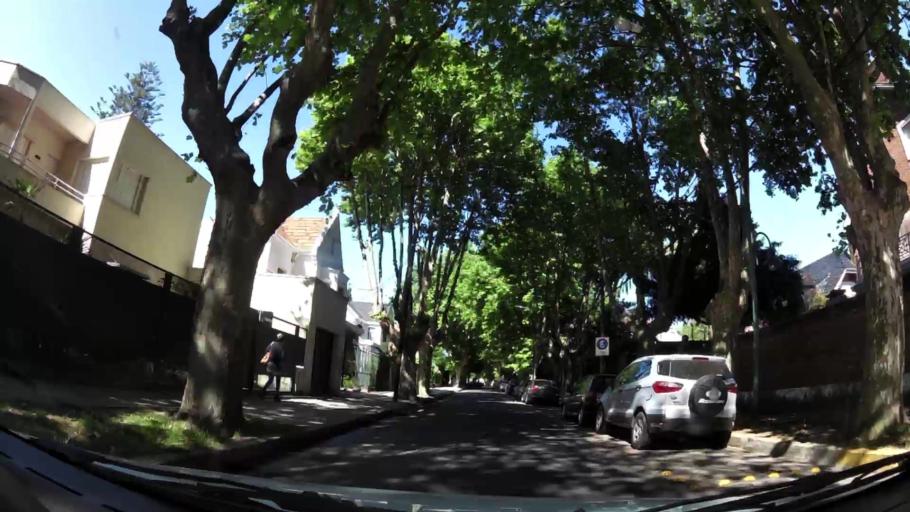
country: AR
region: Buenos Aires
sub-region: Partido de Vicente Lopez
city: Olivos
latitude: -34.5251
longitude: -58.4789
